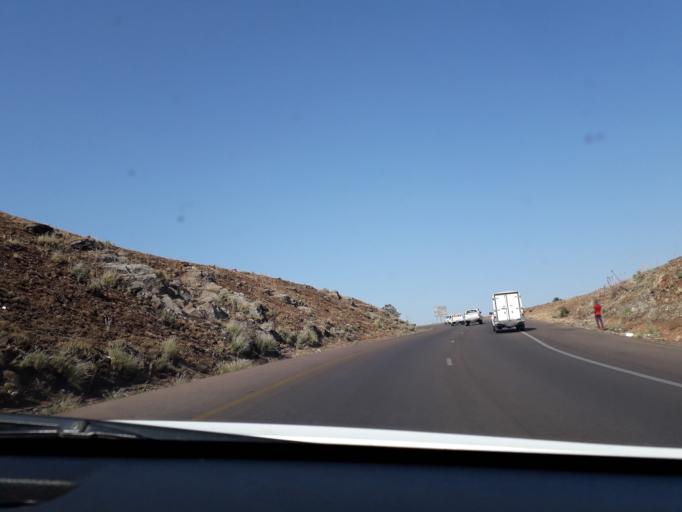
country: ZA
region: Gauteng
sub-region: City of Tshwane Metropolitan Municipality
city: Pretoria
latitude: -25.7855
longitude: 28.1919
